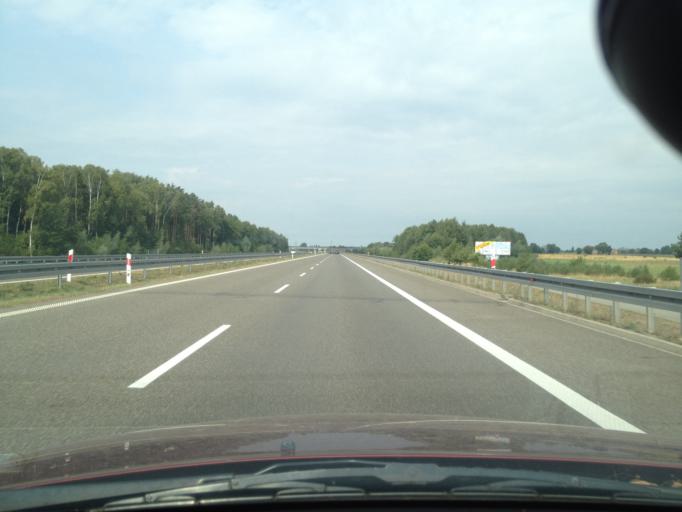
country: PL
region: West Pomeranian Voivodeship
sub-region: Powiat mysliborski
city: Nowogrodek Pomorski
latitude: 52.9341
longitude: 14.9822
